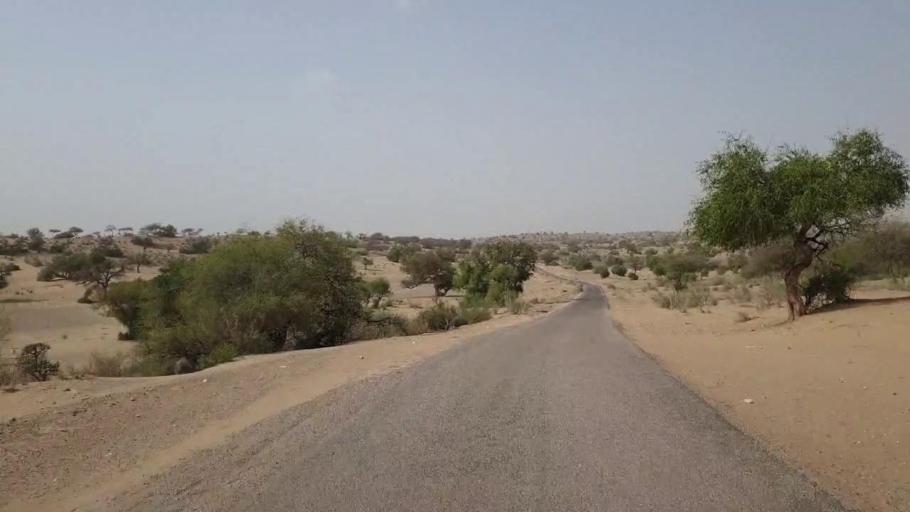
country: PK
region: Sindh
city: Mithi
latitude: 24.5889
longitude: 69.9228
